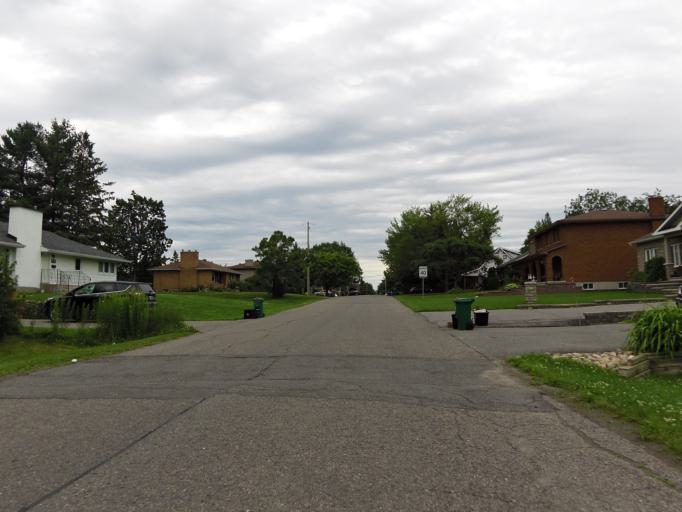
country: CA
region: Ontario
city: Ottawa
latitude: 45.3450
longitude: -75.7434
